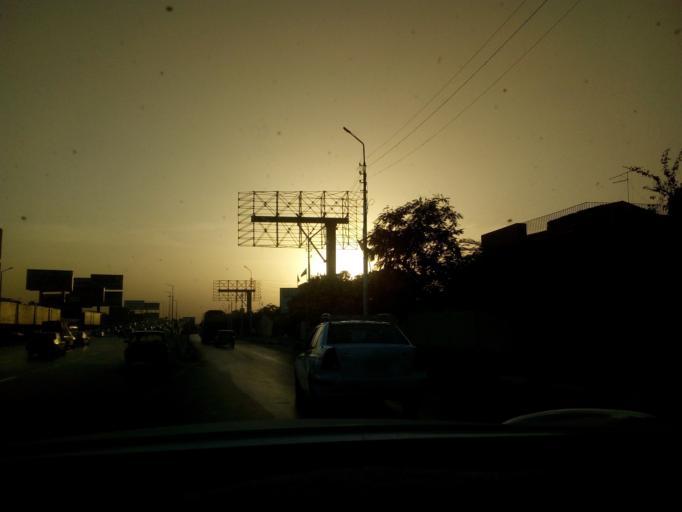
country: EG
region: Muhafazat al Qahirah
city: Cairo
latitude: 30.0977
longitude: 31.3457
